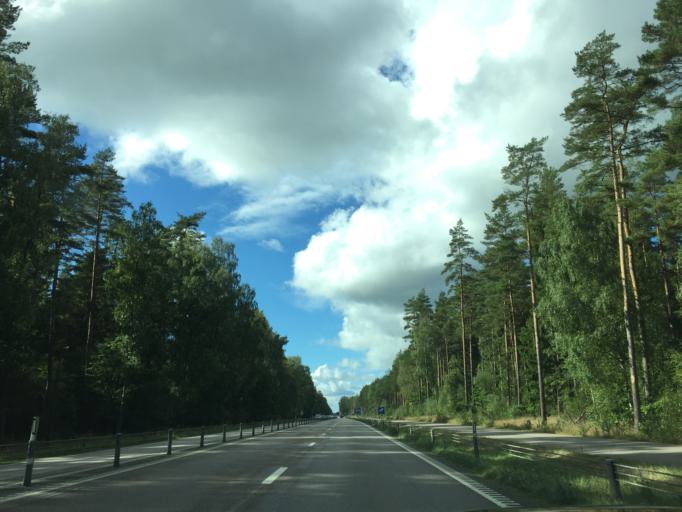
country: SE
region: Skane
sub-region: Sjobo Kommun
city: Sjoebo
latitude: 55.6369
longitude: 13.6614
